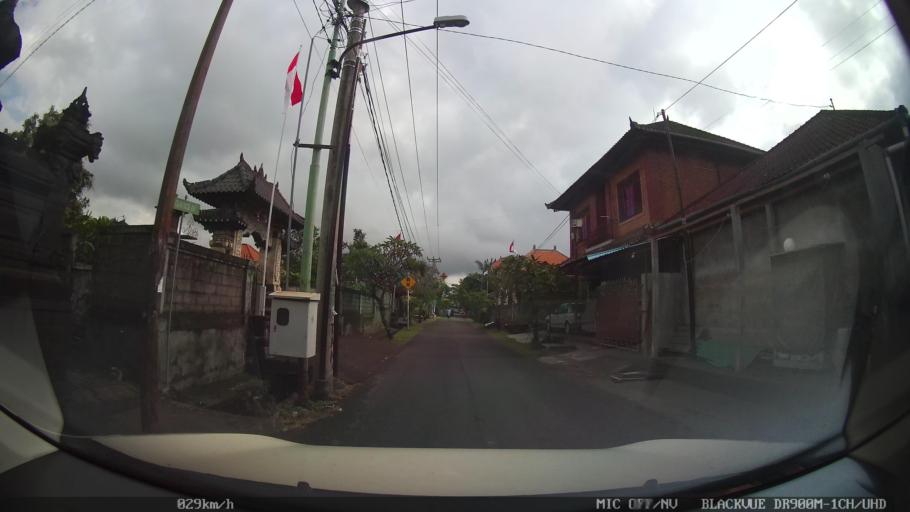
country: ID
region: Bali
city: Banjar Bucu
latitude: -8.5886
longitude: 115.2052
